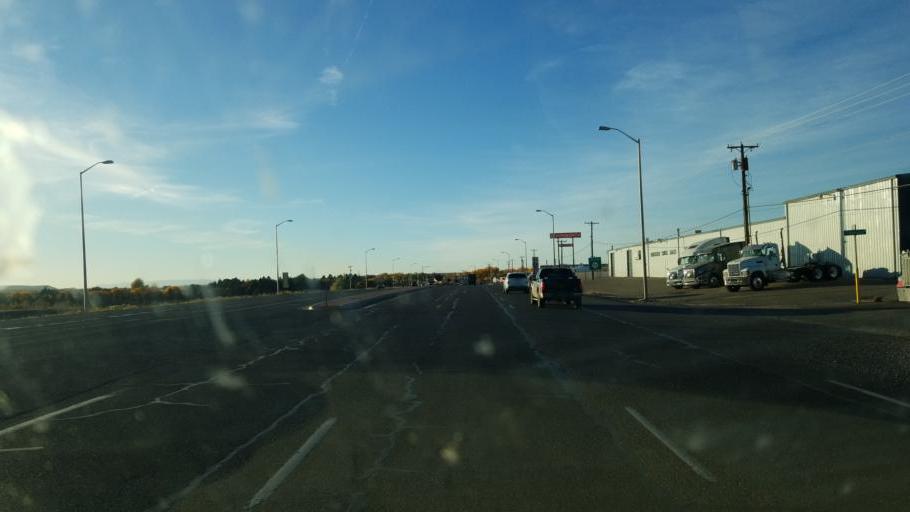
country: US
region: New Mexico
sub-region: San Juan County
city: Farmington
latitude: 36.7169
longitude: -108.1536
